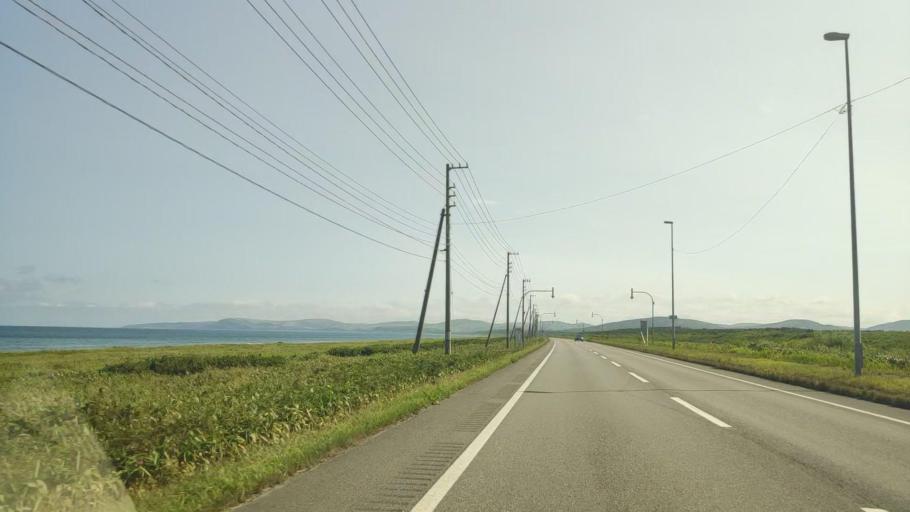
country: JP
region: Hokkaido
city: Makubetsu
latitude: 45.4111
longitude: 141.8131
